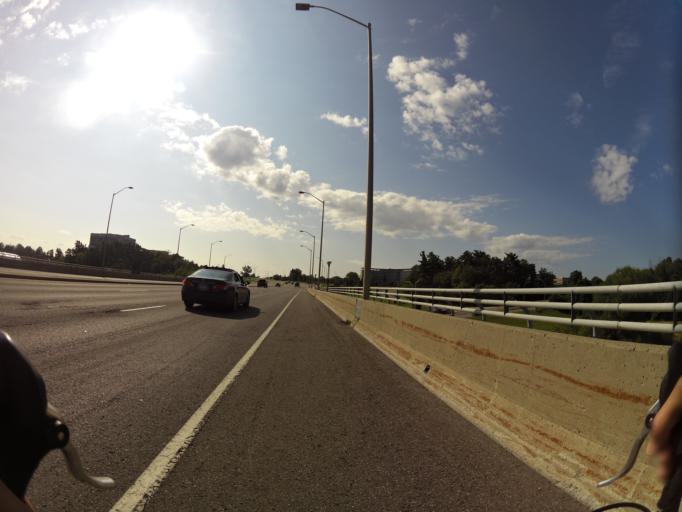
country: CA
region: Ontario
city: Ottawa
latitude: 45.3827
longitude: -75.6885
